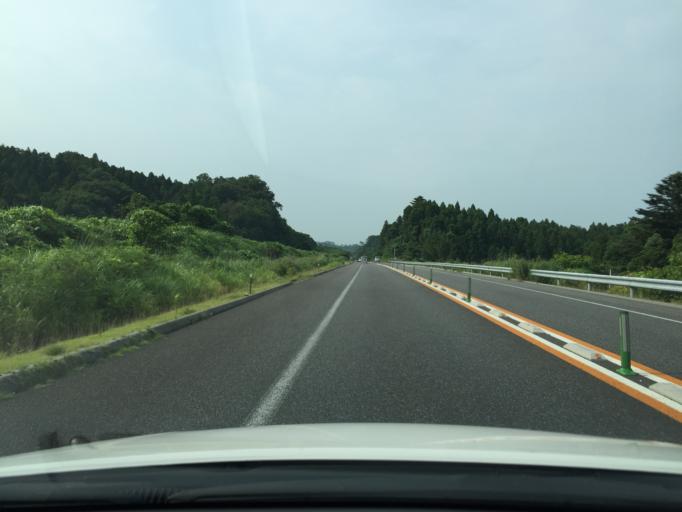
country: JP
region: Fukushima
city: Iwaki
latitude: 37.1543
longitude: 140.9663
